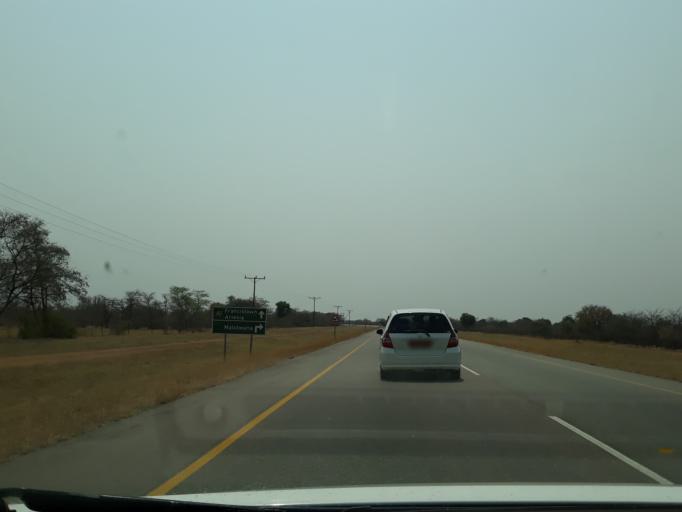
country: BW
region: Kgatleng
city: Mochudi
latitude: -24.2951
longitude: 26.1309
